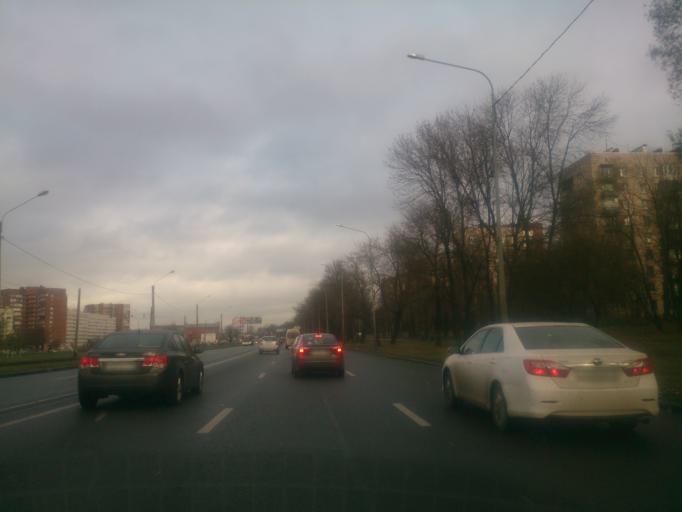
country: RU
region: St.-Petersburg
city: Dachnoye
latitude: 59.8564
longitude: 30.2486
